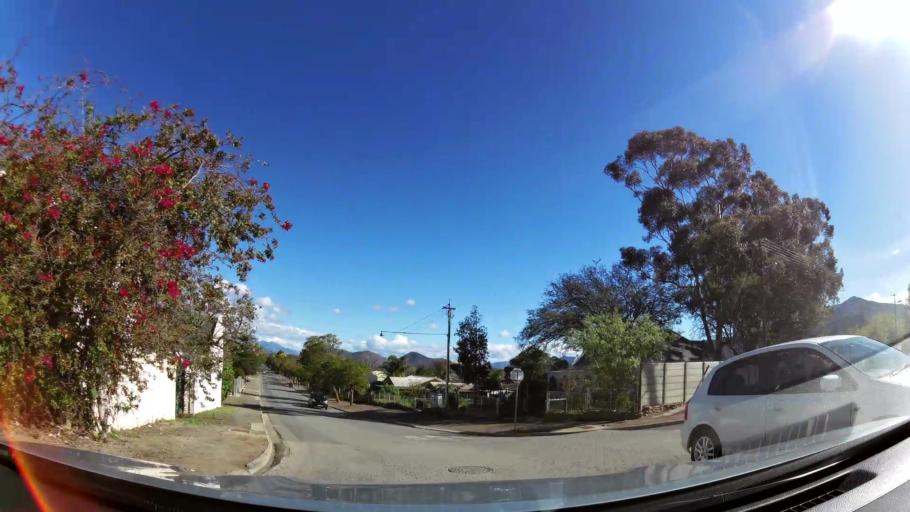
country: ZA
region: Western Cape
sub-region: Cape Winelands District Municipality
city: Ashton
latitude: -33.7959
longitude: 19.8917
